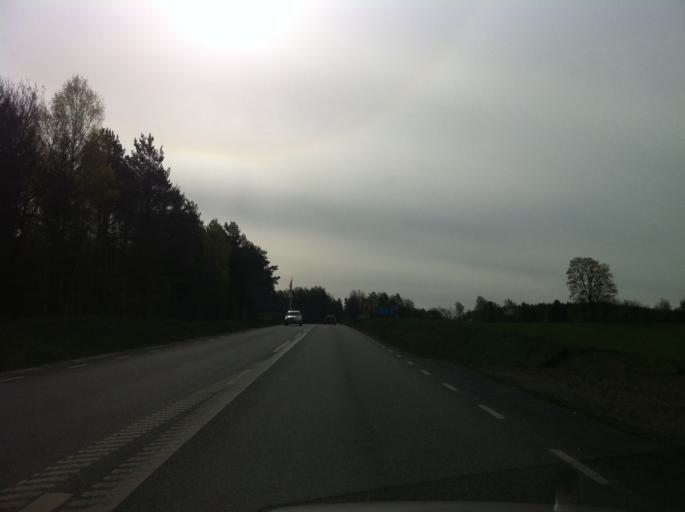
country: SE
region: Vaestra Goetaland
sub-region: Harryda Kommun
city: Ravlanda
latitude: 57.5536
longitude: 12.5239
